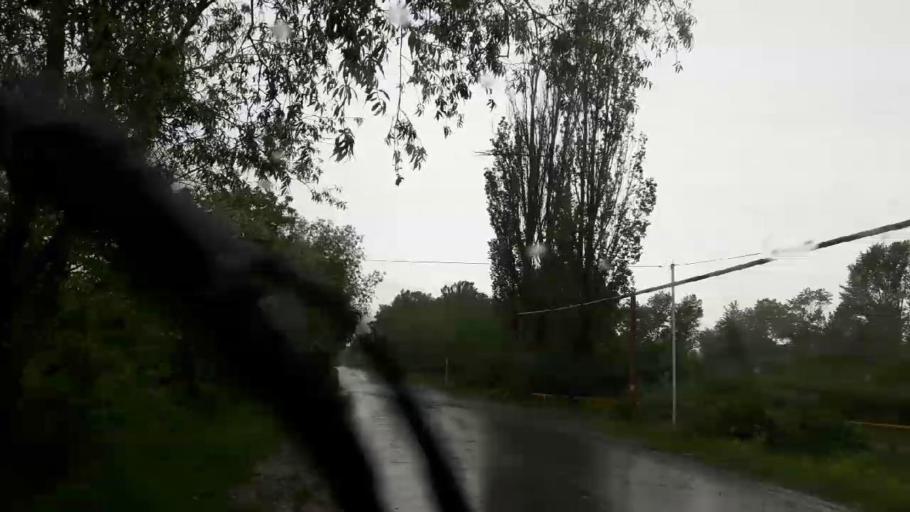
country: GE
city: Agara
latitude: 42.0111
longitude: 43.8582
